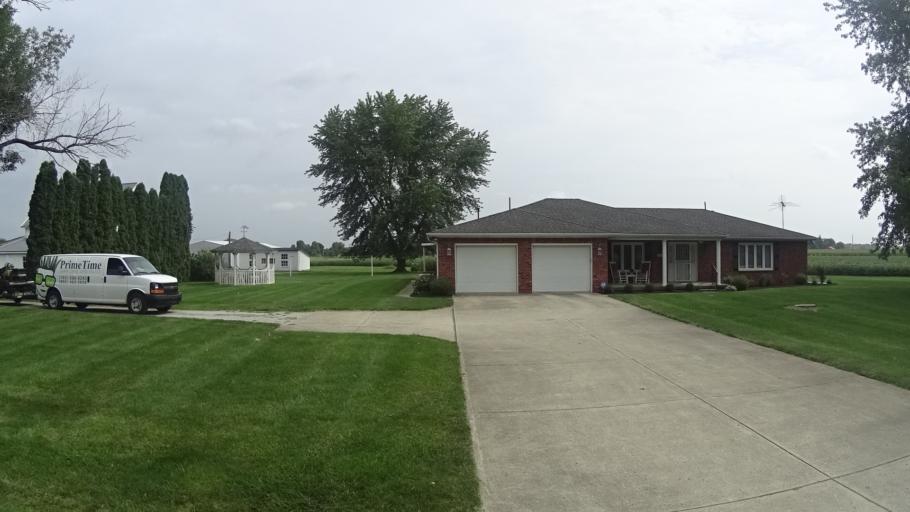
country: US
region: Indiana
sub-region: Madison County
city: Pendleton
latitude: 40.0232
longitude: -85.7753
